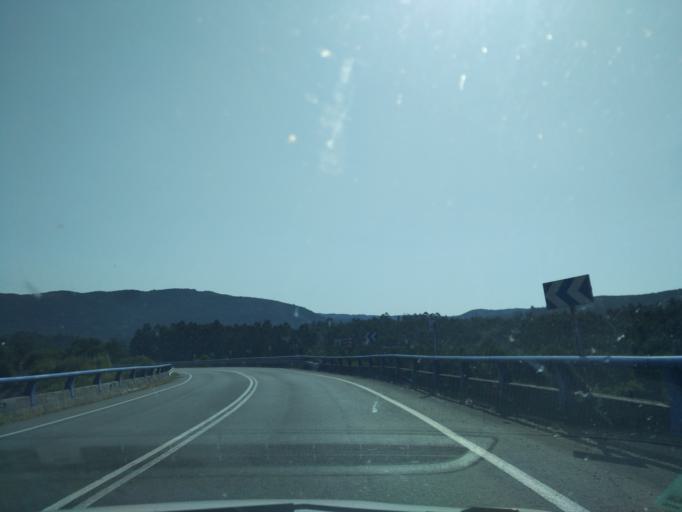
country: ES
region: Galicia
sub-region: Provincia da Coruna
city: Padron
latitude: 42.7293
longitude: -8.6536
